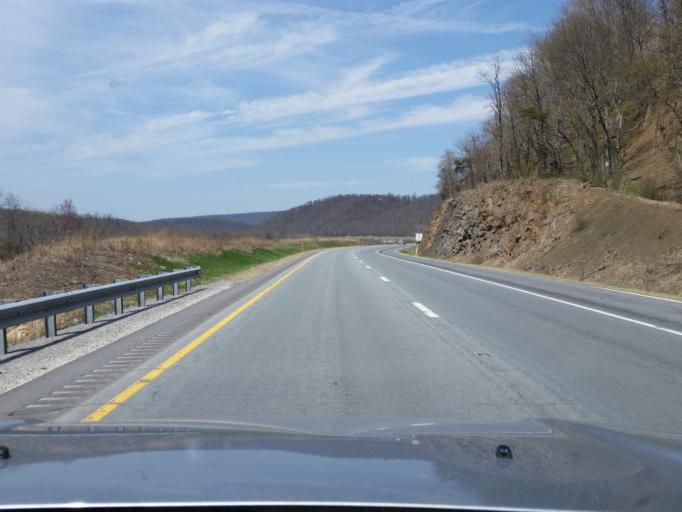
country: US
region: Pennsylvania
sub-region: Perry County
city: Duncannon
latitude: 40.4612
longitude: -77.0270
